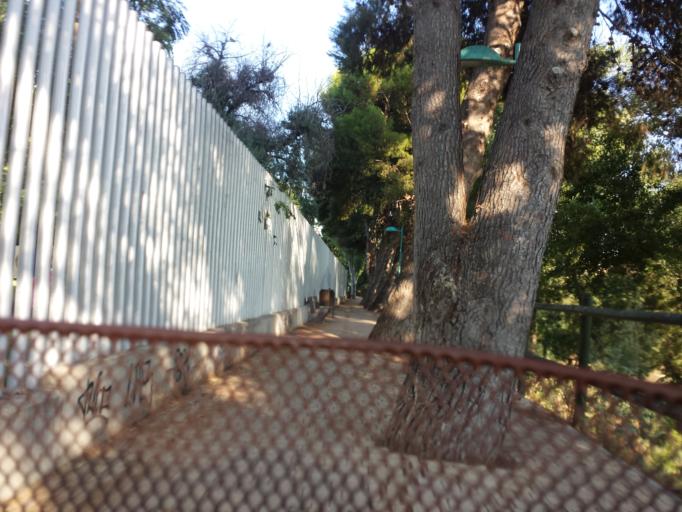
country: ES
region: Aragon
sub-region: Provincia de Zaragoza
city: Zaragoza
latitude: 41.6605
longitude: -0.8870
